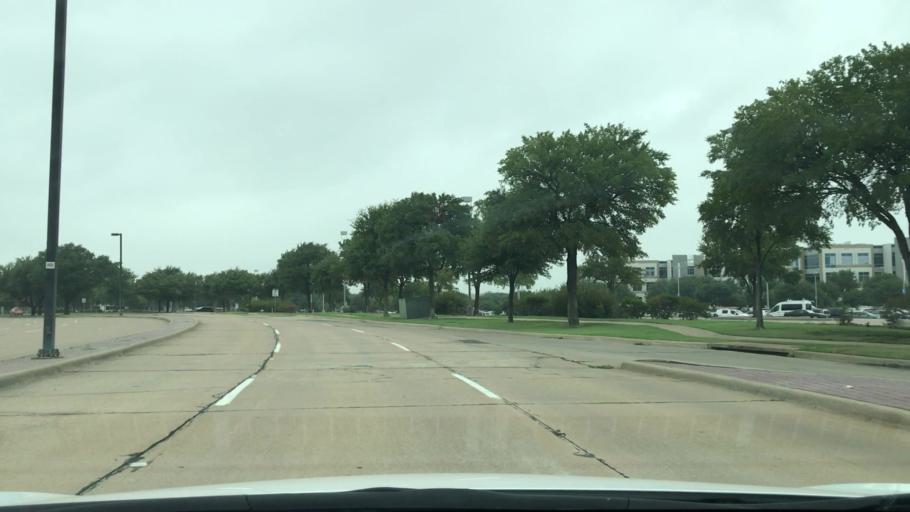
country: US
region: Texas
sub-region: Dallas County
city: Coppell
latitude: 32.9202
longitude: -96.9998
